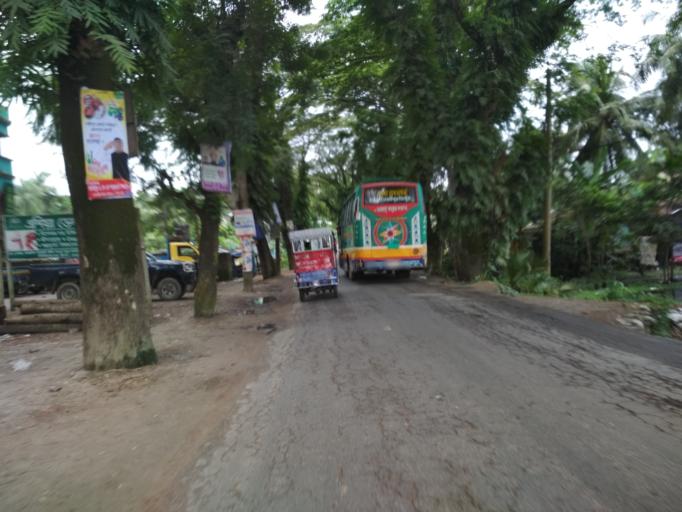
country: BD
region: Chittagong
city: Lakshmipur
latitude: 22.9464
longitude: 90.8116
